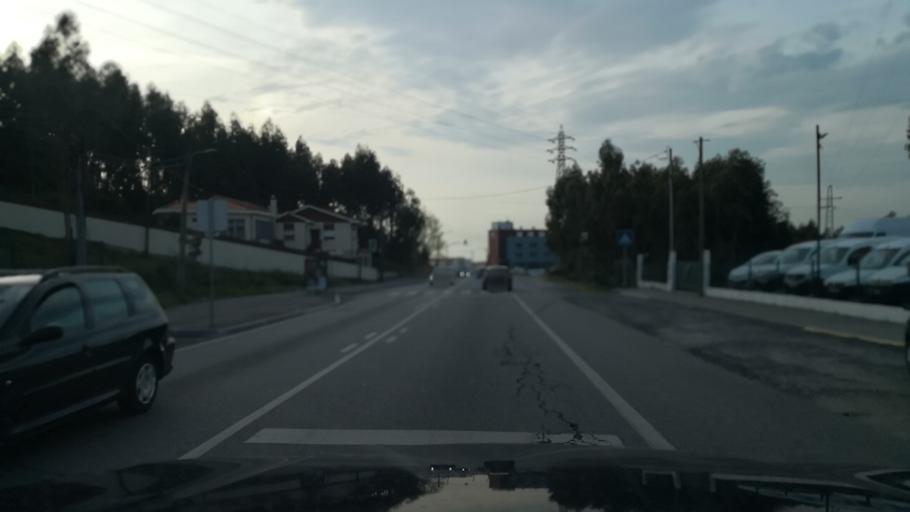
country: PT
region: Porto
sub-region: Gondomar
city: Baguim do Monte
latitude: 41.2059
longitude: -8.5295
